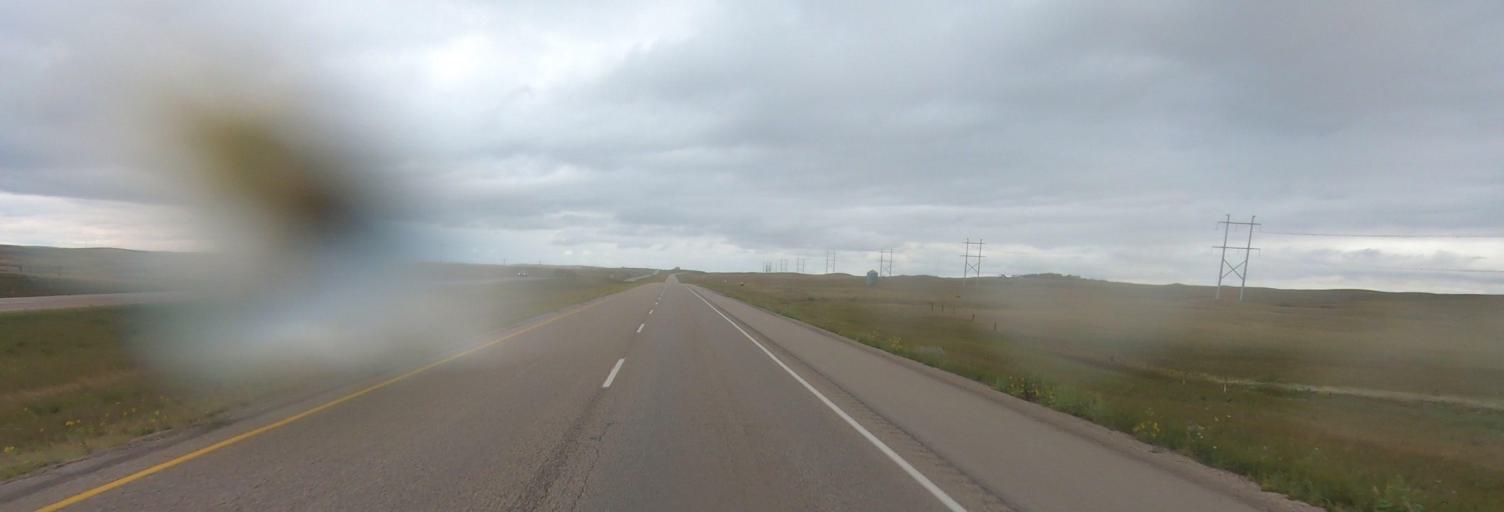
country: CA
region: Saskatchewan
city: Gravelbourg
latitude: 50.4631
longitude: -106.4123
